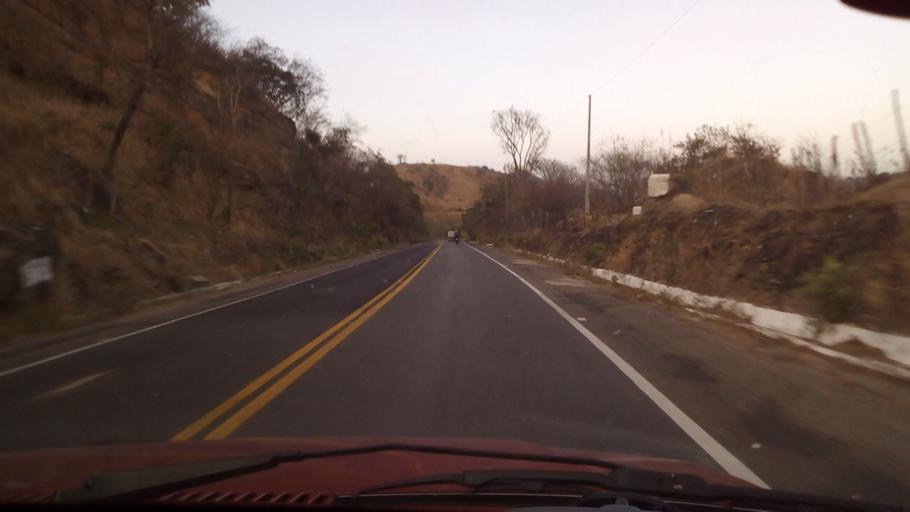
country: BR
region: Paraiba
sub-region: Bananeiras
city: Solanea
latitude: -6.7317
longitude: -35.5548
